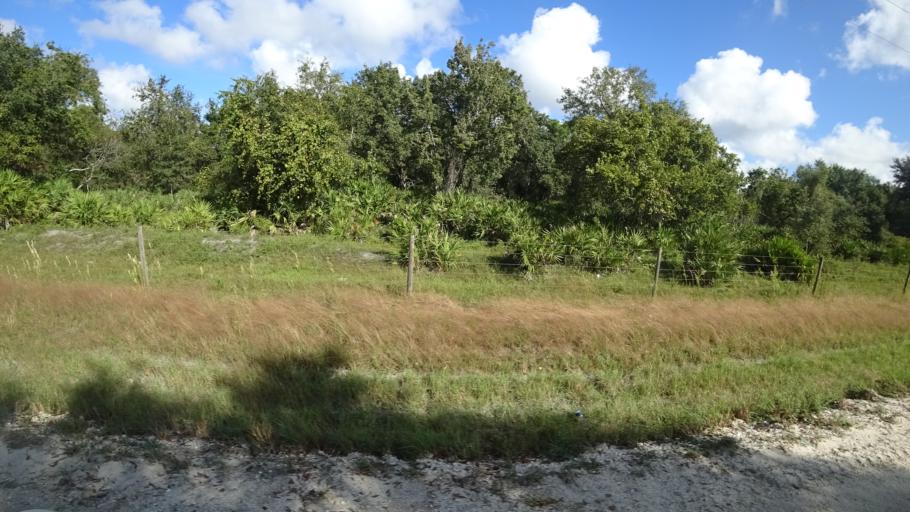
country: US
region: Florida
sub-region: Sarasota County
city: Lake Sarasota
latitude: 27.3249
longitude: -82.2077
